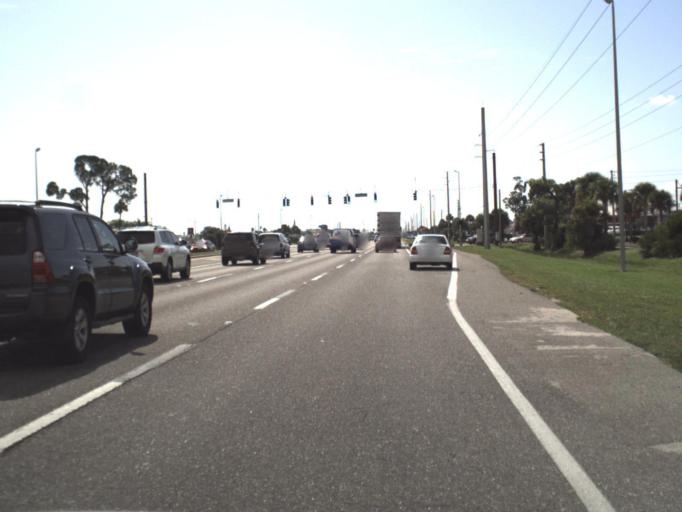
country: US
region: Florida
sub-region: Charlotte County
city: Port Charlotte
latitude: 26.9885
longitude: -82.1080
